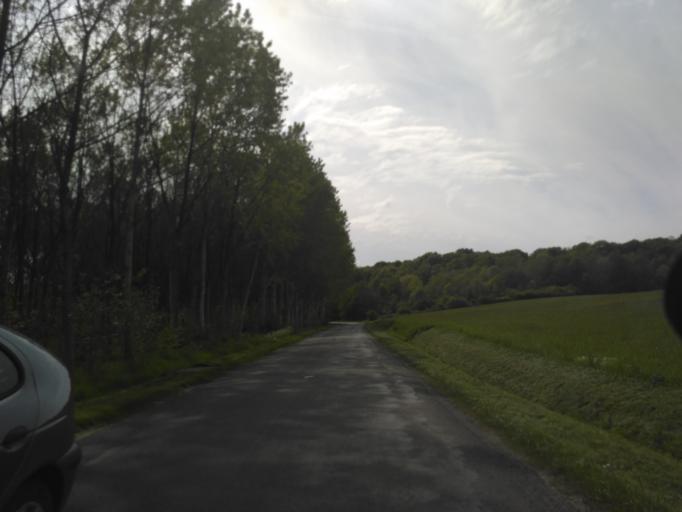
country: FR
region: Ile-de-France
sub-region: Departement de Seine-et-Marne
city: Chaumes-en-Brie
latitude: 48.6664
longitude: 2.8203
